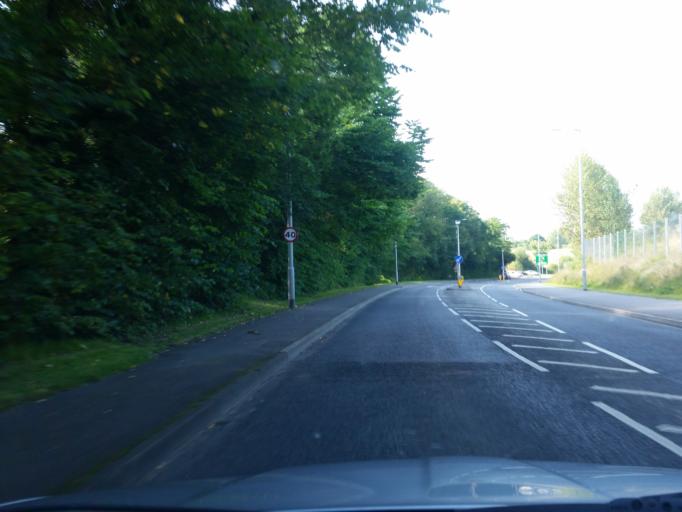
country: GB
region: Northern Ireland
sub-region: Fermanagh District
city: Enniskillen
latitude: 54.3569
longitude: -7.6289
